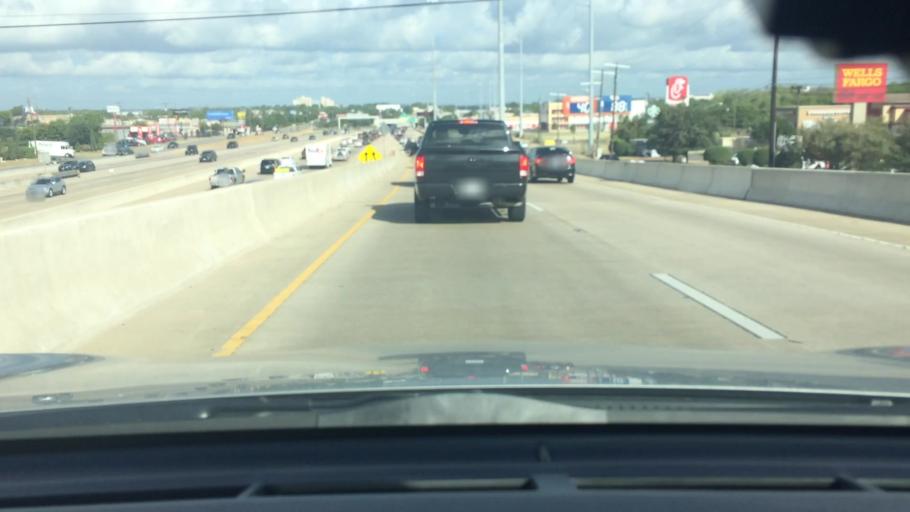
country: US
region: Texas
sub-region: Travis County
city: Austin
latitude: 30.2192
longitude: -97.7582
